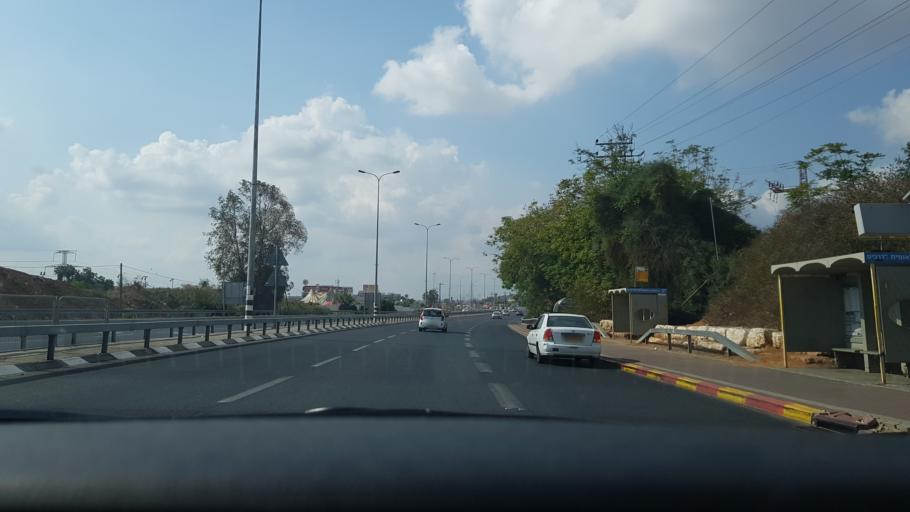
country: IL
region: Central District
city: Mazkeret Batya
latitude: 31.8703
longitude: 34.8188
